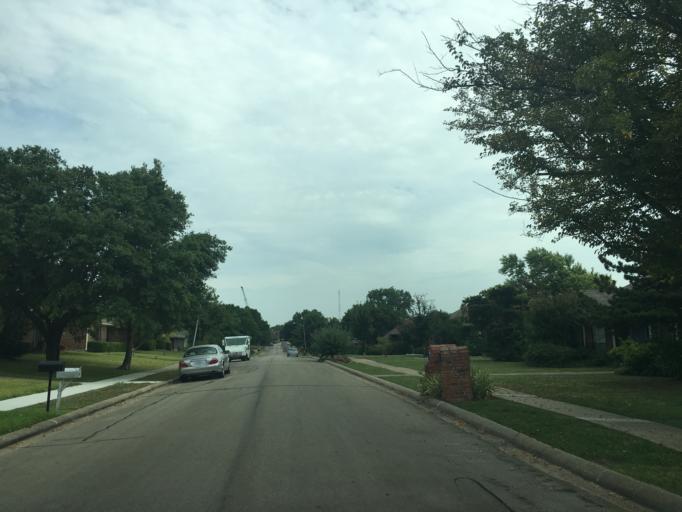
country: US
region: Texas
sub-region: Collin County
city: Wylie
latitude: 33.0140
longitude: -96.5296
